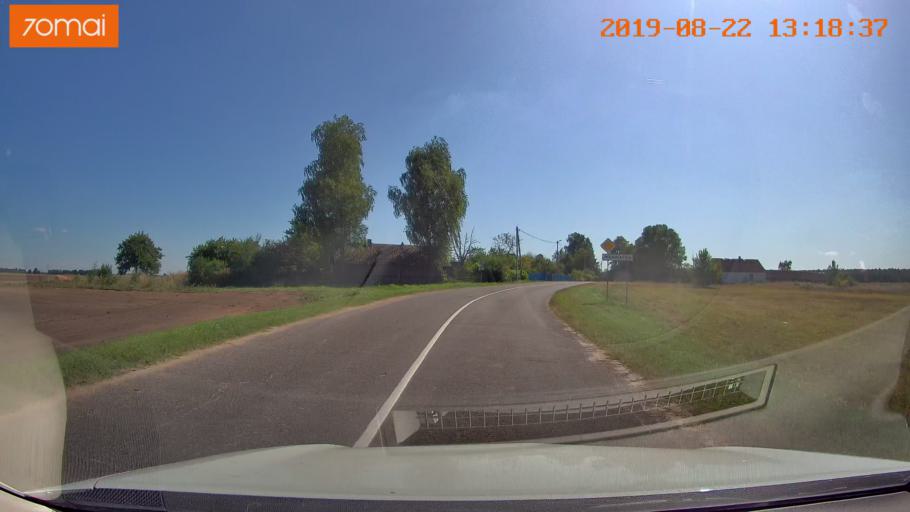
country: BY
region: Minsk
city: Urechcha
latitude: 53.2397
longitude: 27.9417
